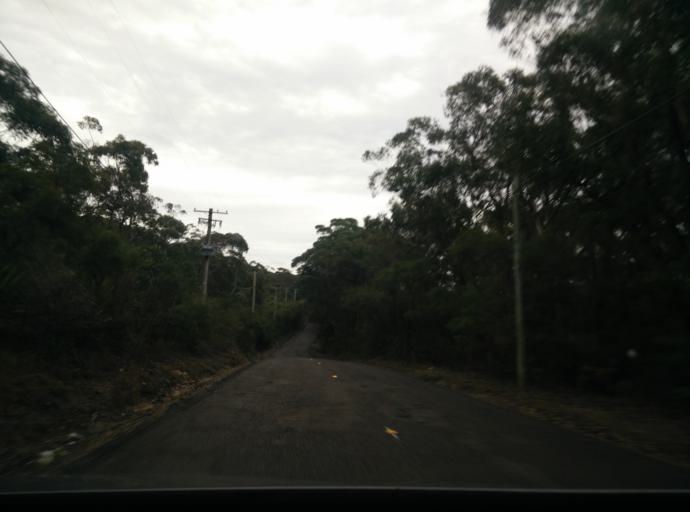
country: AU
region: New South Wales
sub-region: Gosford Shire
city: Narara
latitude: -33.3538
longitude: 151.2979
